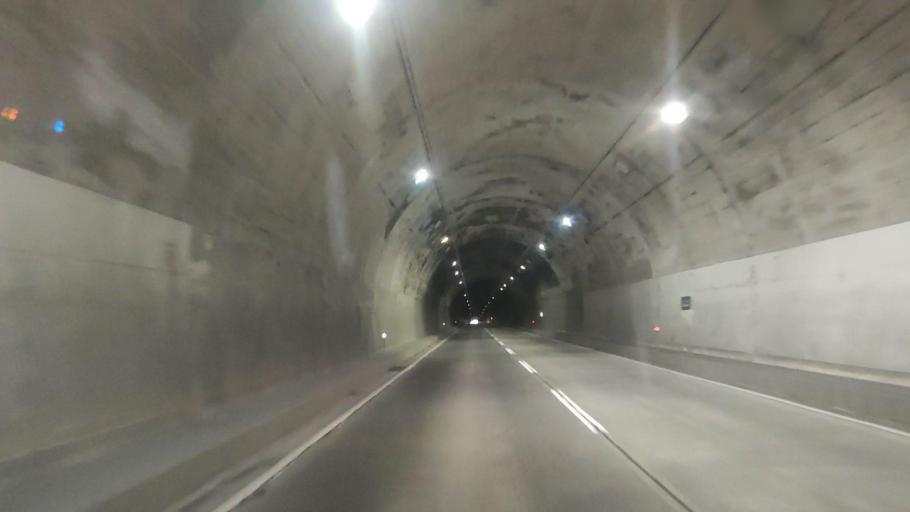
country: JP
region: Kagoshima
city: Okuchi-shinohara
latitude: 31.9762
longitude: 130.7415
